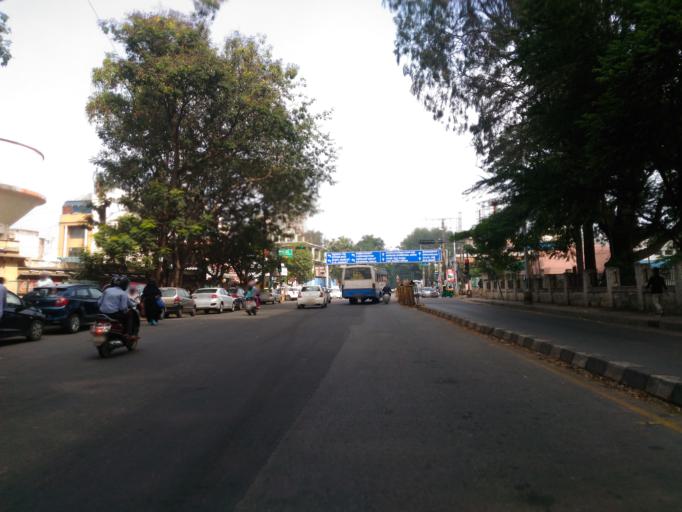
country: IN
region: Karnataka
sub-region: Bangalore Urban
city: Bangalore
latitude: 12.9638
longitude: 77.6068
